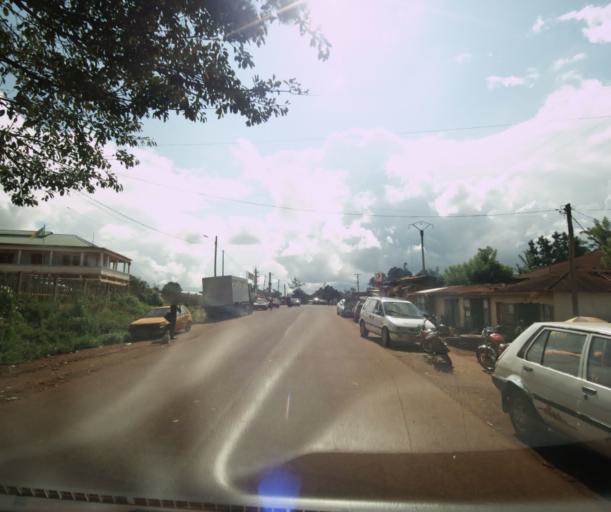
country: CM
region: West
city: Foumban
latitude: 5.7313
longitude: 10.8787
